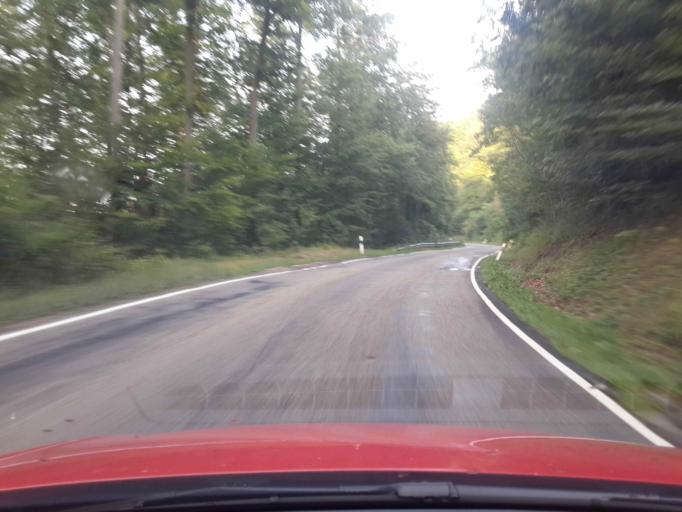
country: DE
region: Baden-Wuerttemberg
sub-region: Regierungsbezirk Stuttgart
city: Pfaffenhofen
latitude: 49.0420
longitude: 8.9763
